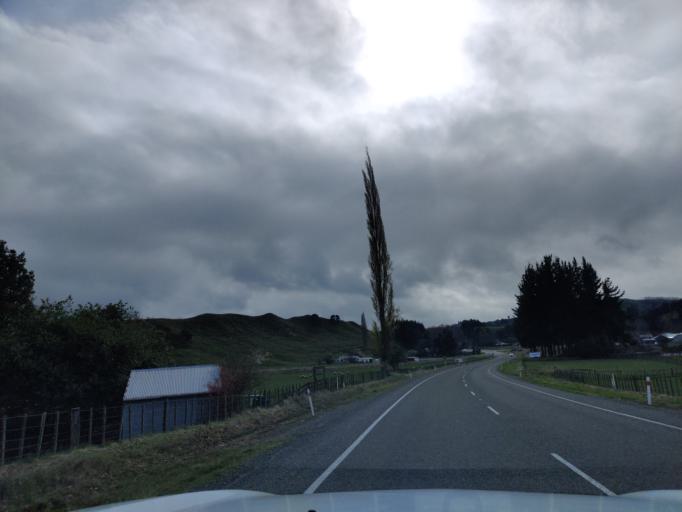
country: NZ
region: Manawatu-Wanganui
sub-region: Ruapehu District
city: Waiouru
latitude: -39.7373
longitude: 175.8407
